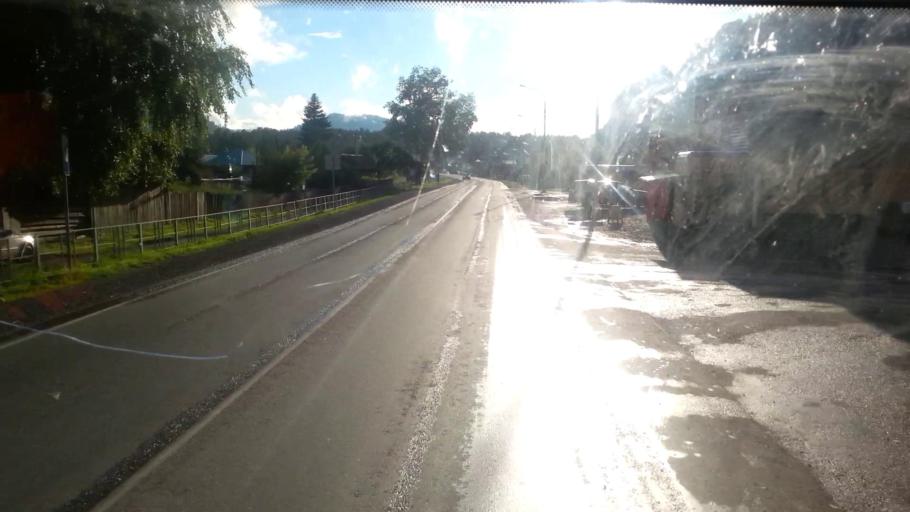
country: RU
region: Altay
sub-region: Mayminskiy Rayon
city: Manzherok
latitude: 51.8338
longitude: 85.7756
